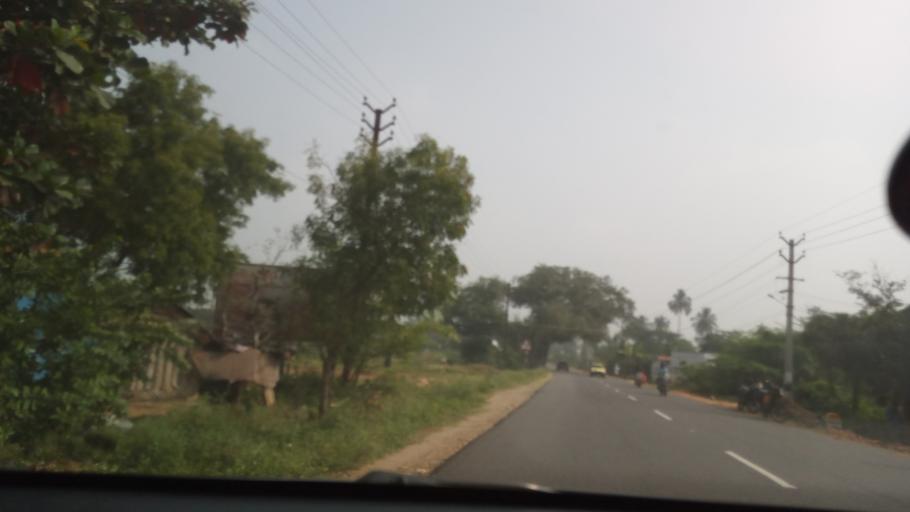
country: IN
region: Tamil Nadu
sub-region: Erode
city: Punjai Puliyampatti
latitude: 11.3278
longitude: 77.1499
